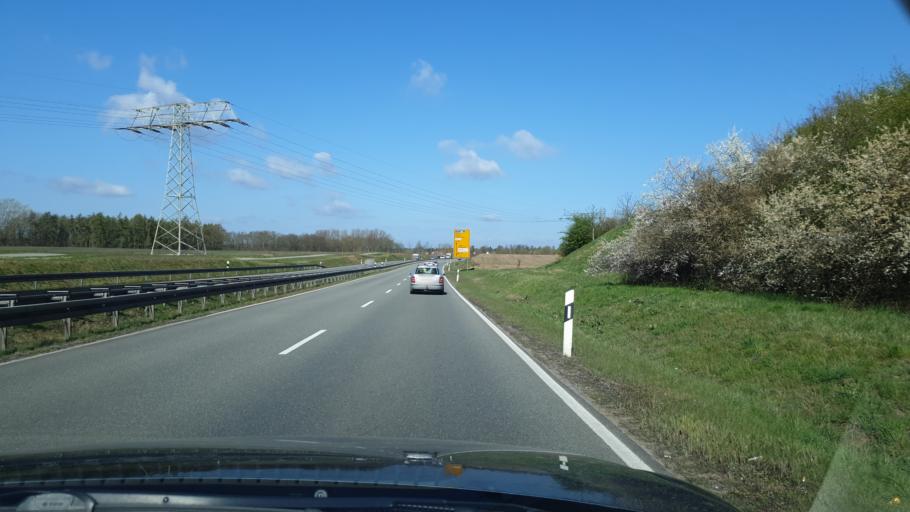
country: DE
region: Mecklenburg-Vorpommern
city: Lankow
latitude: 53.6404
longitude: 11.3511
